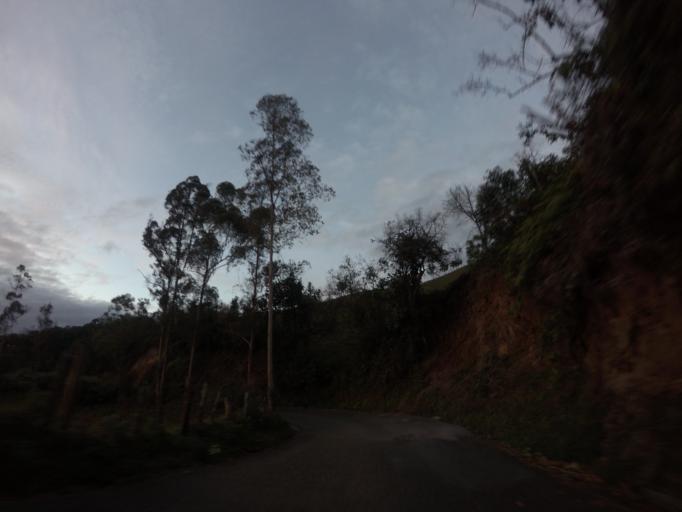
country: CO
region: Caldas
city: Manzanares
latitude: 5.2688
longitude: -75.1286
